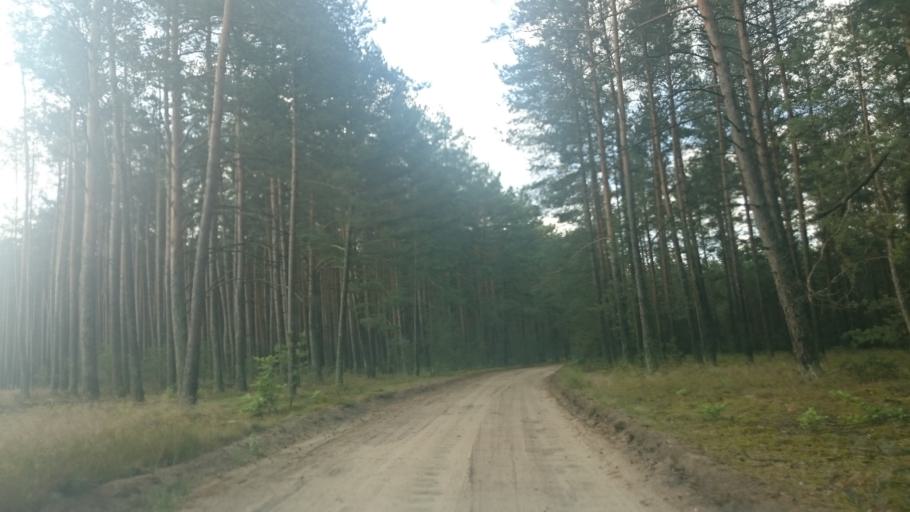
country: PL
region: Pomeranian Voivodeship
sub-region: Powiat koscierski
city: Karsin
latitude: 53.9907
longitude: 17.9340
